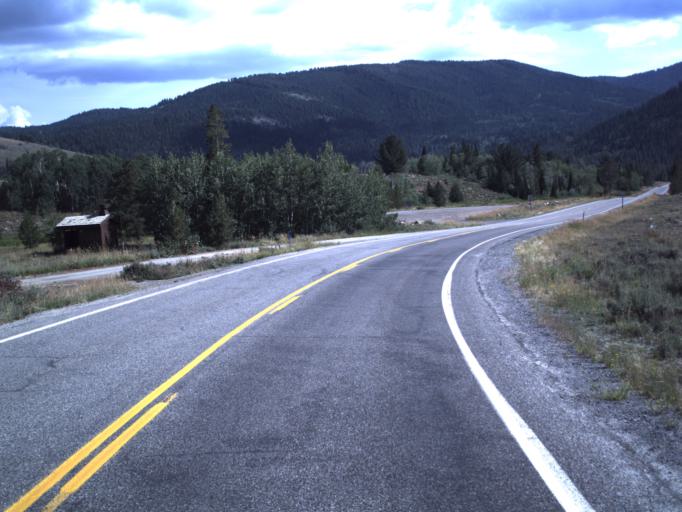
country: US
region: Idaho
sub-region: Bear Lake County
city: Paris
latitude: 41.9743
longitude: -111.5322
